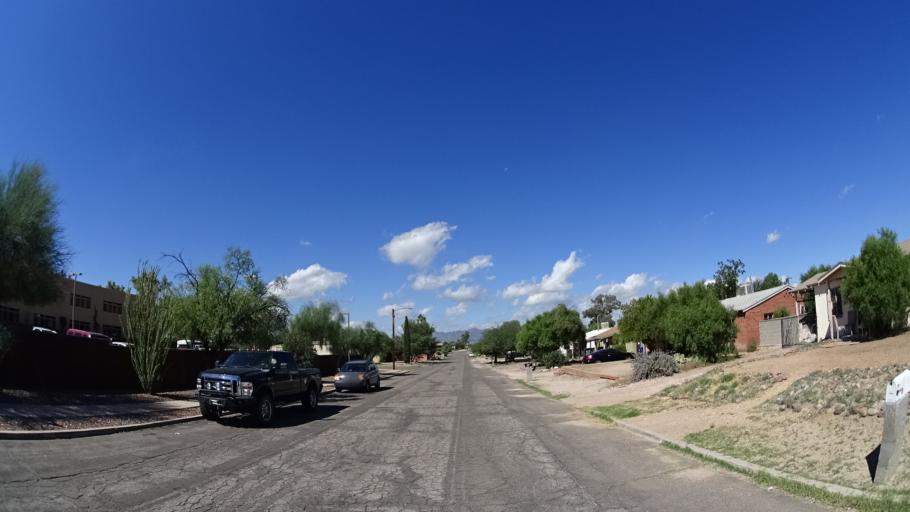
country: US
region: Arizona
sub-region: Pima County
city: Tucson
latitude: 32.2468
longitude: -110.9573
